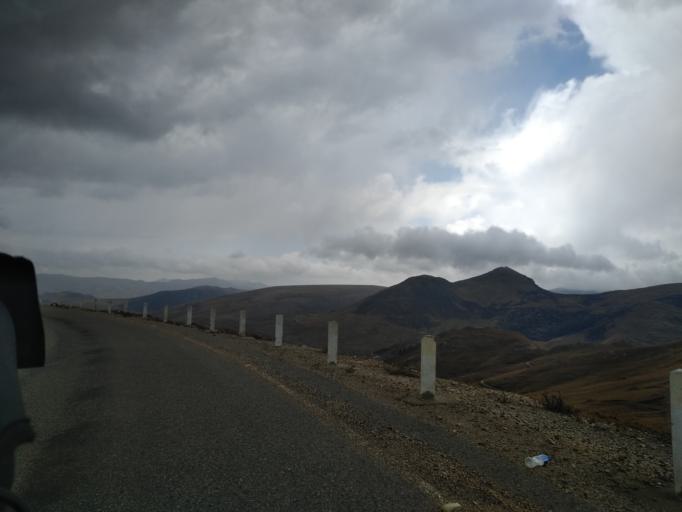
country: PE
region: La Libertad
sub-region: Provincia de Santiago de Chuco
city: Quiruvilca
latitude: -7.9931
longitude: -78.3054
